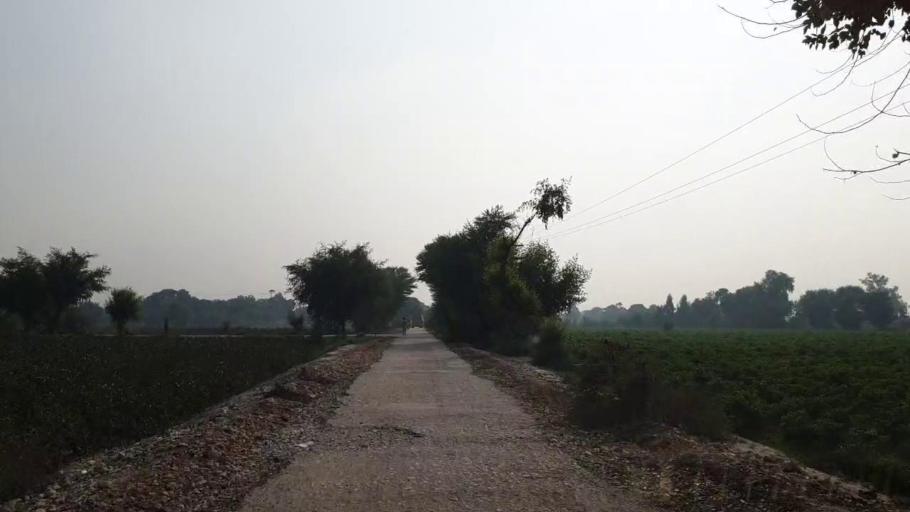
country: PK
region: Sindh
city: Bhan
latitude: 26.5837
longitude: 67.7305
